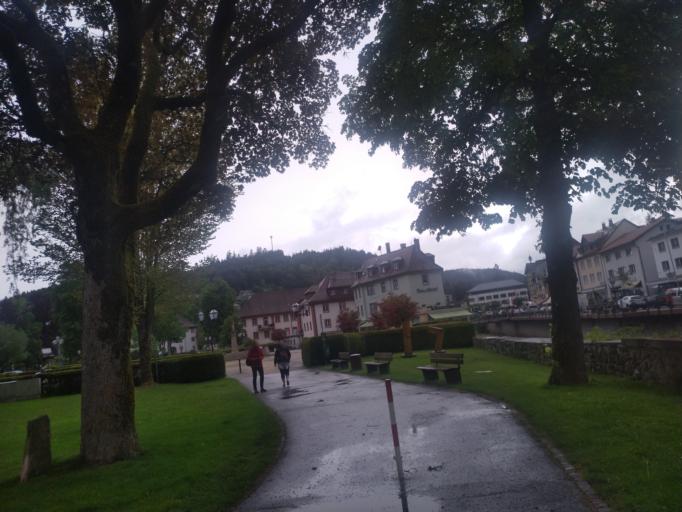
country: DE
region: Baden-Wuerttemberg
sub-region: Freiburg Region
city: Sankt Blasien
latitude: 47.7606
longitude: 8.1313
